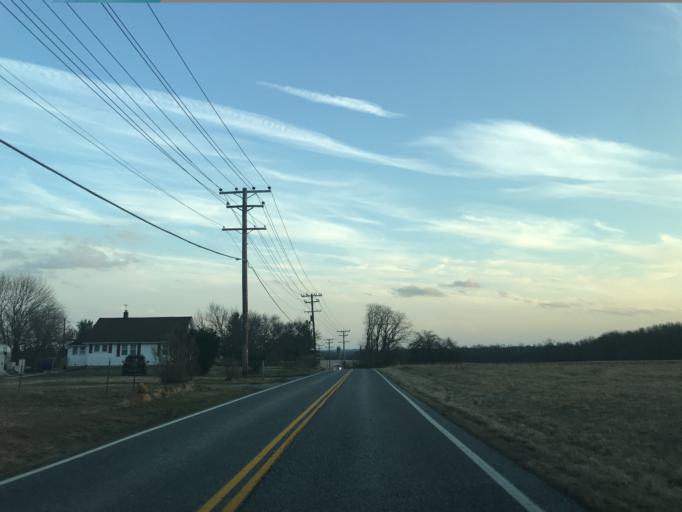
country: US
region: Maryland
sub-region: Harford County
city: Bel Air South
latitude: 39.5249
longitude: -76.2767
